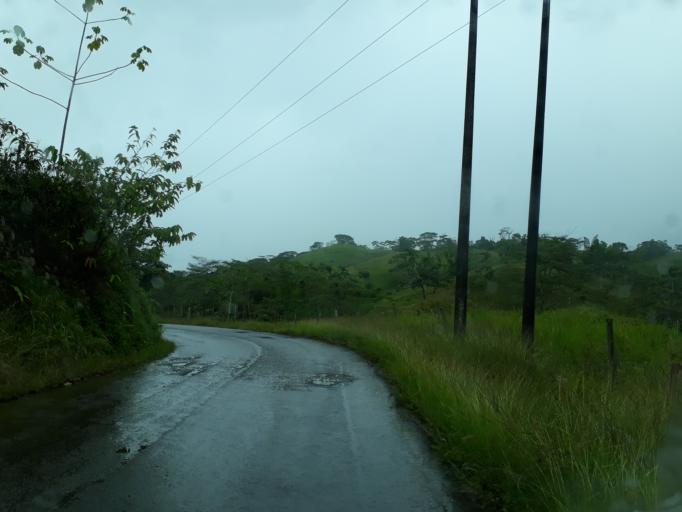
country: CO
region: Cundinamarca
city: Medina
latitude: 4.6580
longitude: -73.3281
